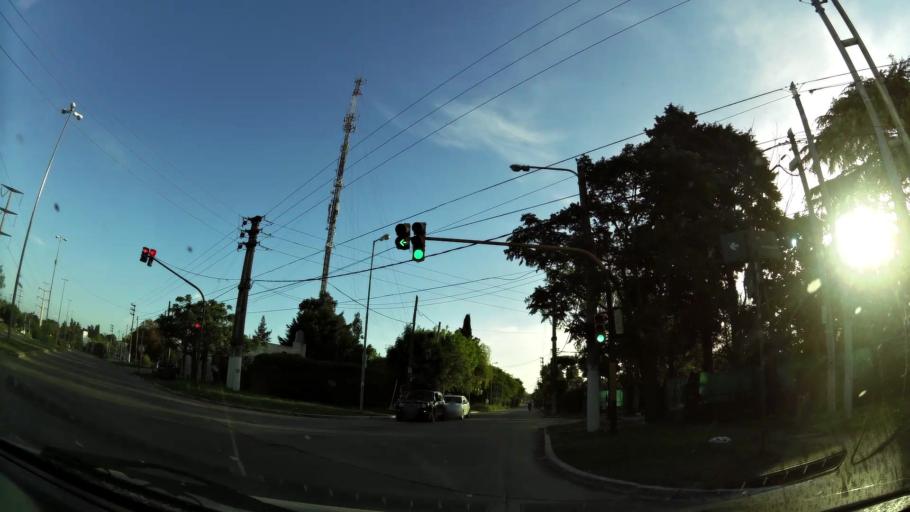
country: AR
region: Buenos Aires
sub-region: Partido de Quilmes
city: Quilmes
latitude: -34.8058
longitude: -58.2066
